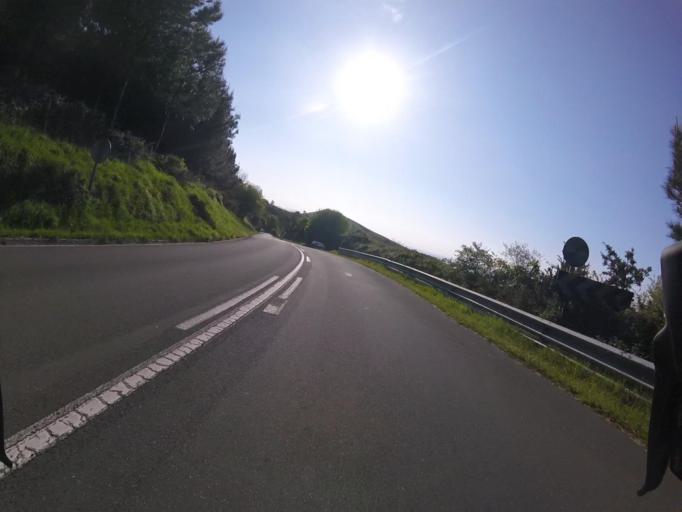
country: ES
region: Basque Country
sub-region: Provincia de Guipuzcoa
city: Lezo
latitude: 43.3360
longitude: -1.8885
